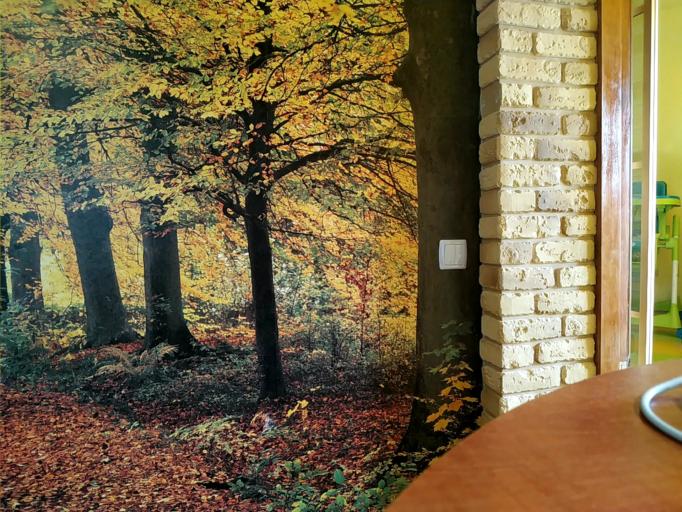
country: RU
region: Tverskaya
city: Kalashnikovo
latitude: 57.3332
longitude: 35.3415
